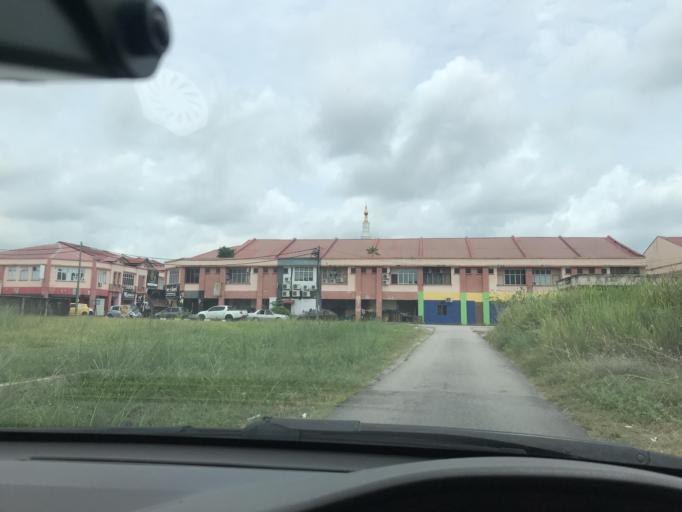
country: MY
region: Kelantan
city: Kota Bharu
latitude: 6.1200
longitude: 102.2186
